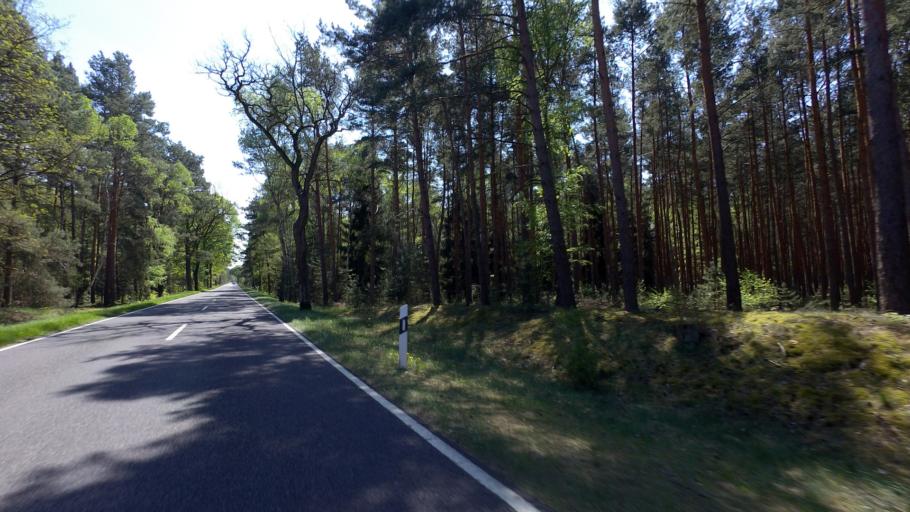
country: DE
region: Brandenburg
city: Halbe
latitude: 52.1596
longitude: 13.7355
